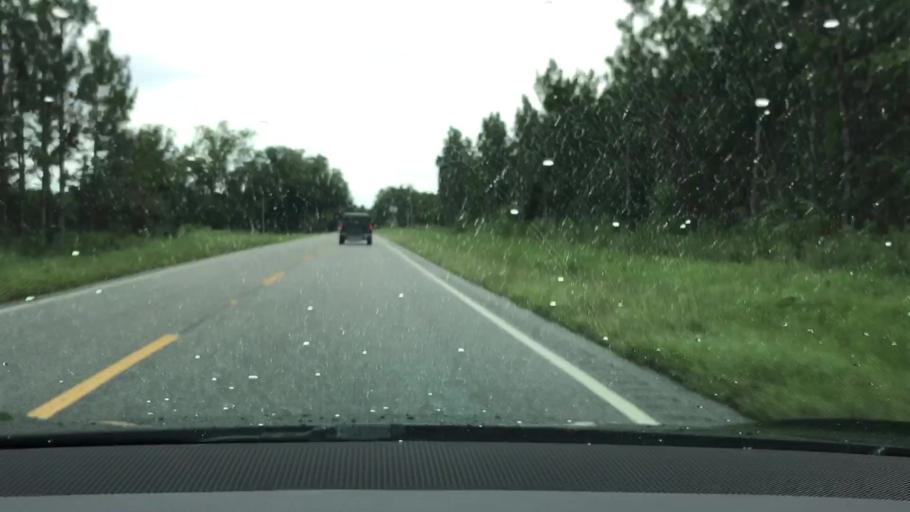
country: US
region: Alabama
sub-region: Geneva County
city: Samson
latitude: 31.0488
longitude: -86.1012
